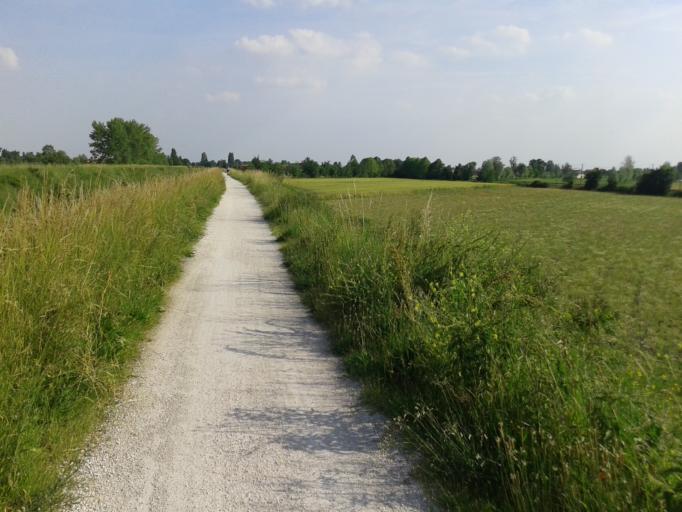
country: IT
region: Veneto
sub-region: Provincia di Padova
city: Loreggiola
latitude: 45.6119
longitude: 11.9294
